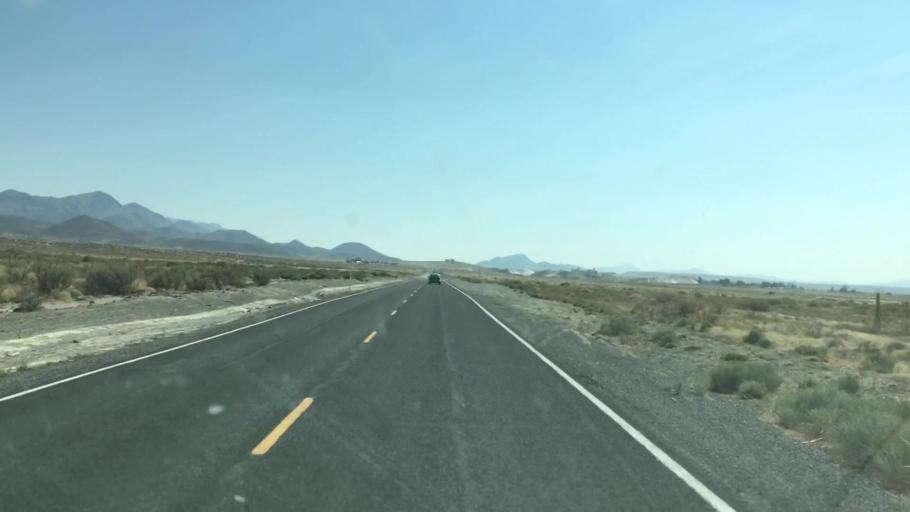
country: US
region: Nevada
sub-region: Pershing County
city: Lovelock
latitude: 40.5989
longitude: -119.3349
